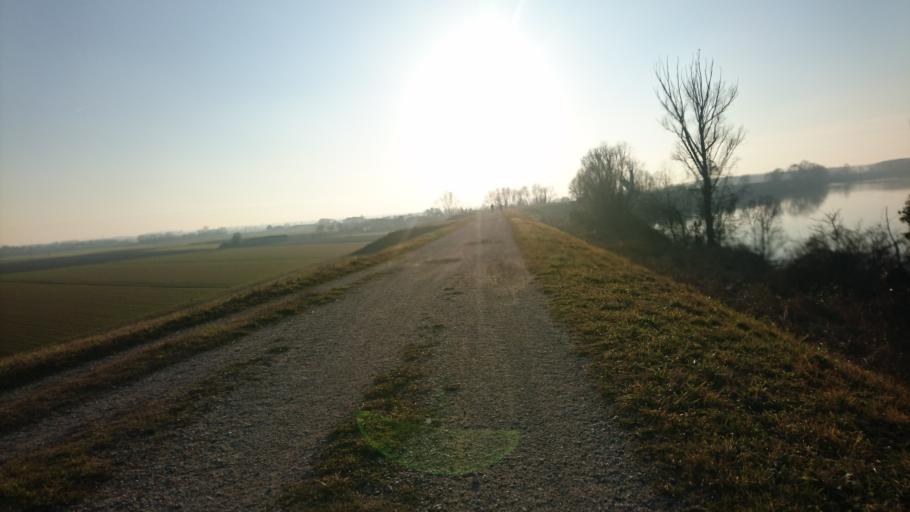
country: IT
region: Veneto
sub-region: Provincia di Rovigo
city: Mardimago
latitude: 45.1228
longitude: 11.8347
